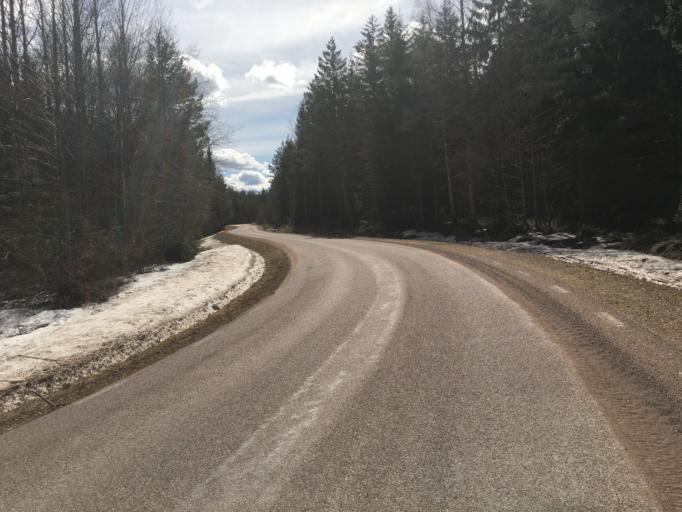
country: SE
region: Gaevleborg
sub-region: Hofors Kommun
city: Hofors
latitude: 60.4871
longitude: 16.4169
